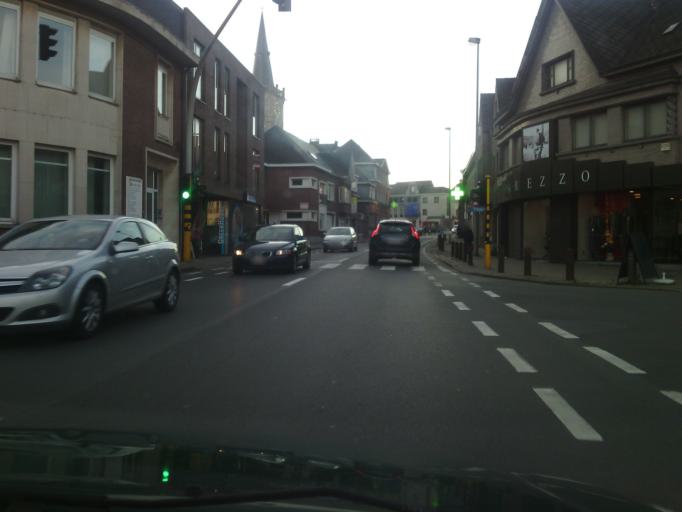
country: BE
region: Flanders
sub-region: Provincie Oost-Vlaanderen
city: Lede
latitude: 50.9674
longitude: 3.9771
